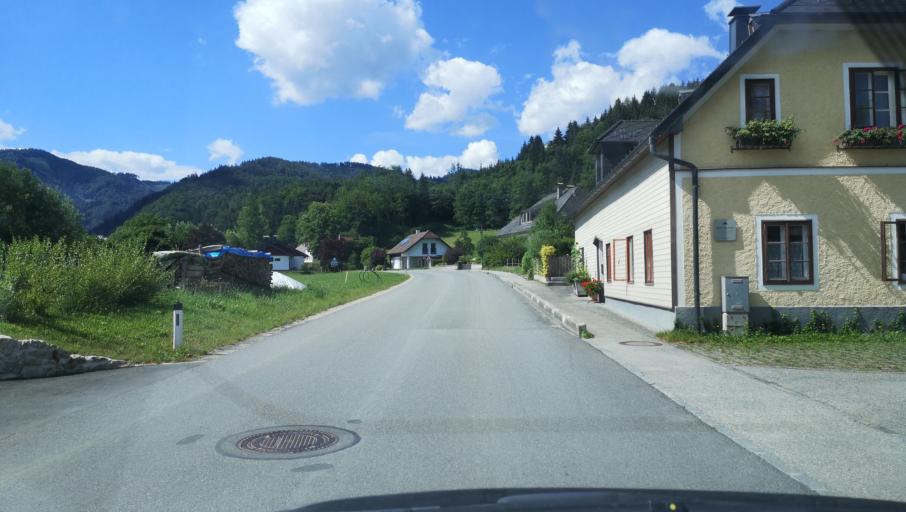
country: AT
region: Lower Austria
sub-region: Politischer Bezirk Scheibbs
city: Gresten
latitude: 47.9501
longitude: 15.0302
